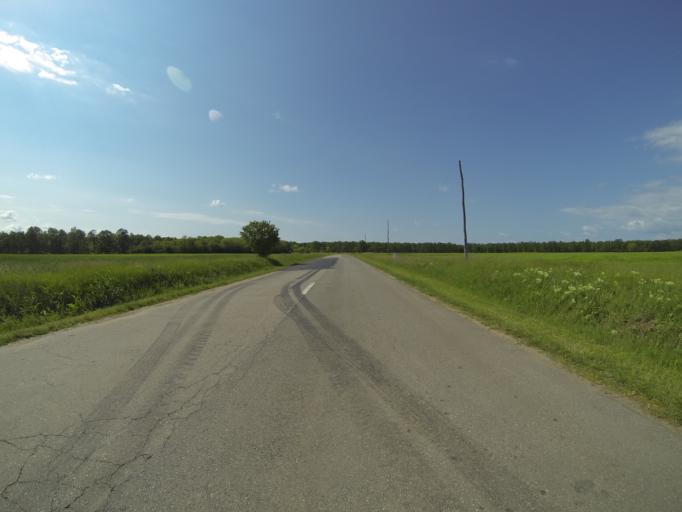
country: RO
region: Dolj
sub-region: Comuna Plenita
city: Plenita
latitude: 44.2386
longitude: 23.1679
